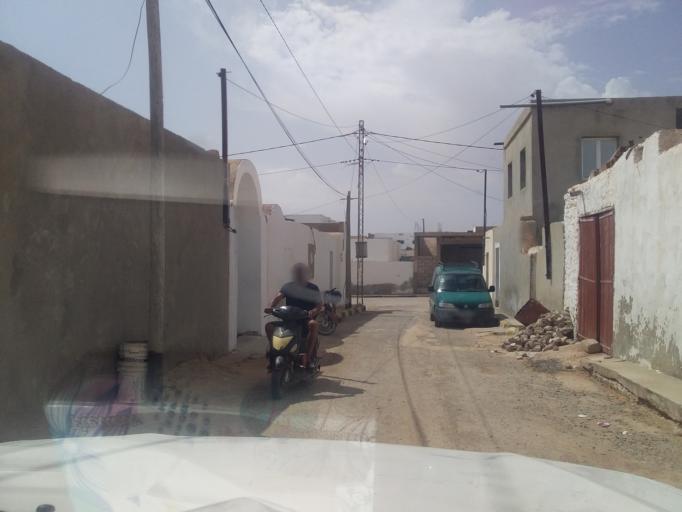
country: TN
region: Madanin
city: Medenine
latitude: 33.5847
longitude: 10.3222
